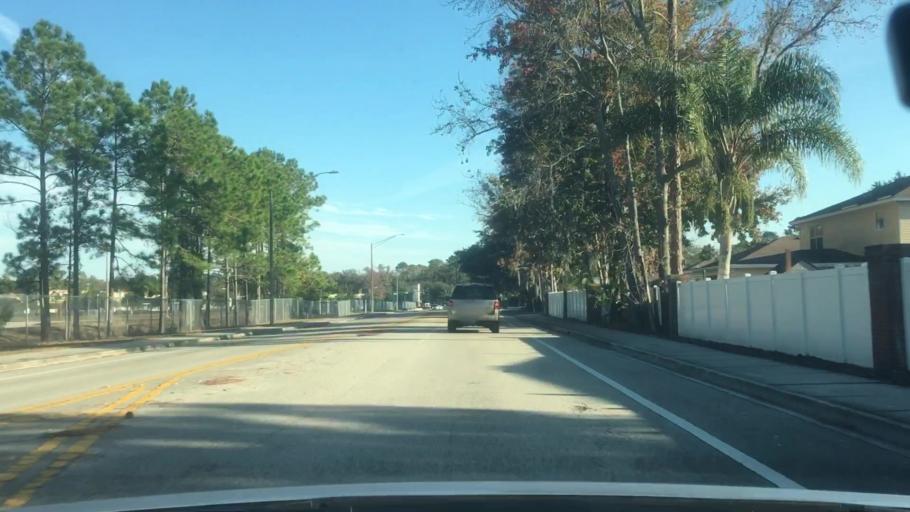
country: US
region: Florida
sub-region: Nassau County
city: Yulee
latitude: 30.4812
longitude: -81.6058
